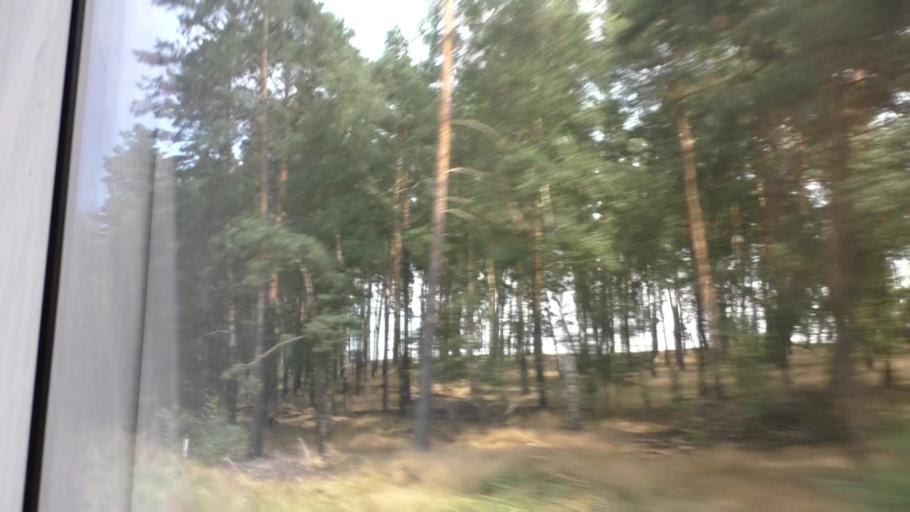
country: DE
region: Brandenburg
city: Mixdorf
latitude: 52.2026
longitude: 14.3991
